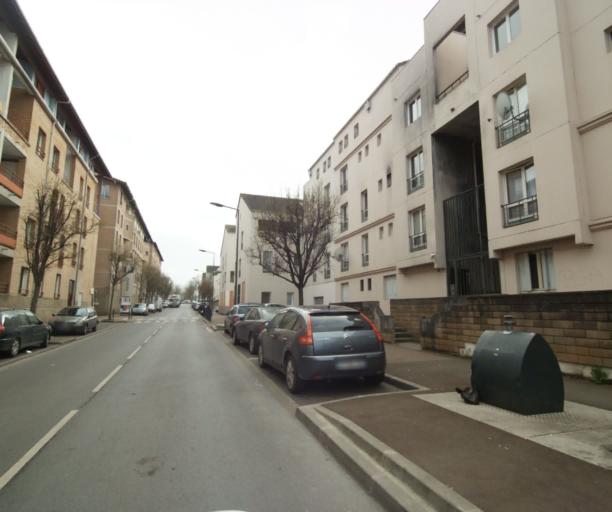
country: FR
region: Ile-de-France
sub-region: Departement du Val-d'Oise
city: Vaureal
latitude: 49.0483
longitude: 2.0326
